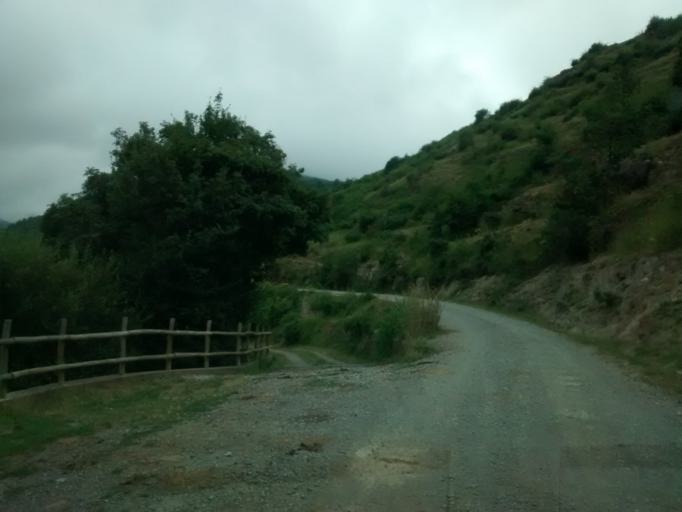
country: ES
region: La Rioja
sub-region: Provincia de La Rioja
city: Ajamil
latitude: 42.1649
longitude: -2.4862
